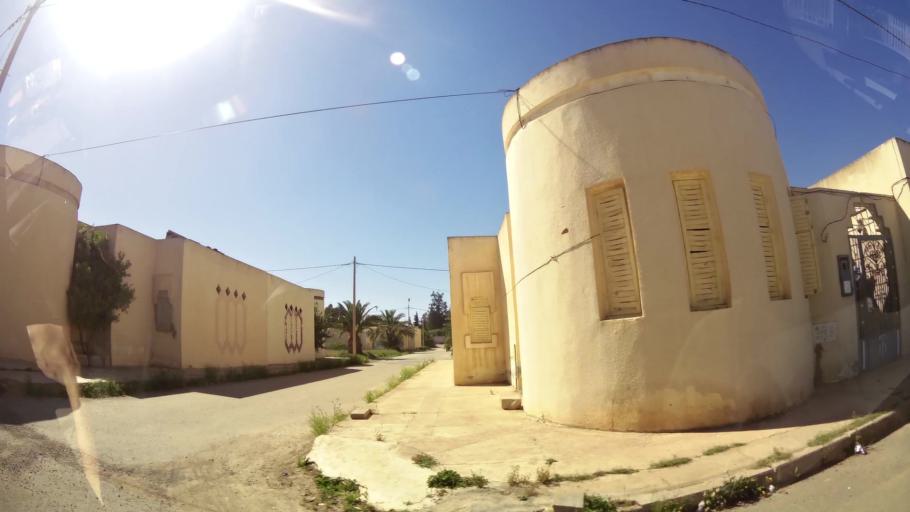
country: MA
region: Oriental
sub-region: Oujda-Angad
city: Oujda
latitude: 34.7213
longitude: -1.9148
